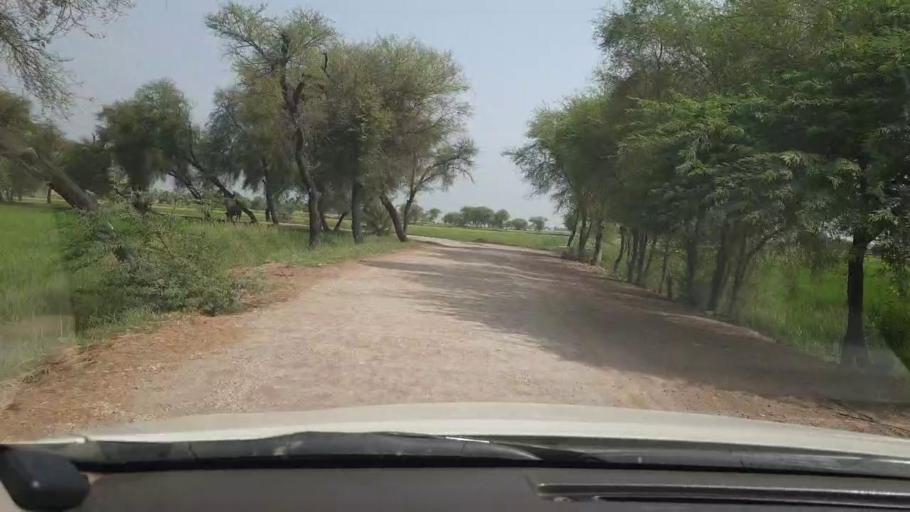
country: PK
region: Sindh
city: Shikarpur
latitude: 27.9999
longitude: 68.5952
